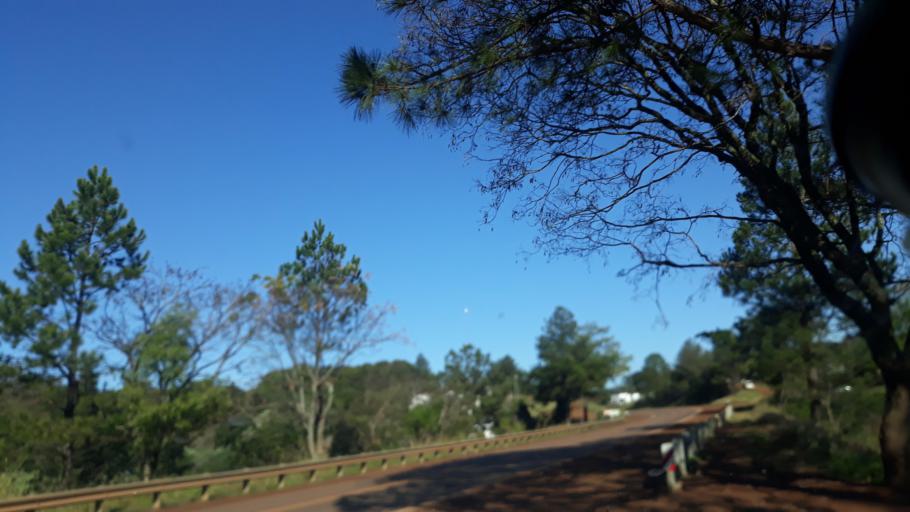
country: AR
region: Misiones
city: Bernardo de Irigoyen
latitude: -26.2674
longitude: -53.6603
